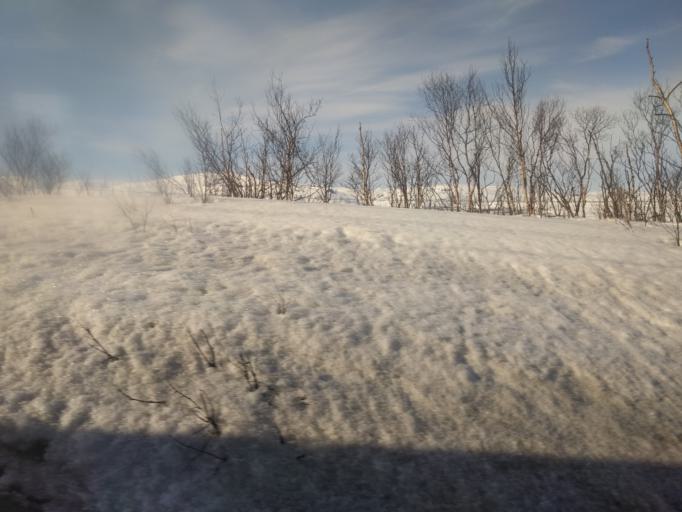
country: NO
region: Troms
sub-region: Bardu
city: Setermoen
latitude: 68.4277
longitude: 18.4016
